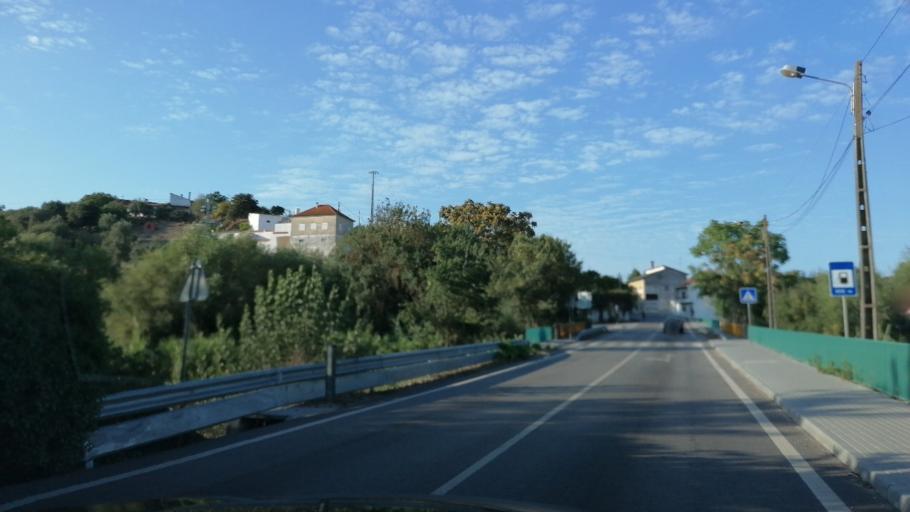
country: PT
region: Santarem
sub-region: Alcanena
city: Alcanena
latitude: 39.3812
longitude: -8.6607
